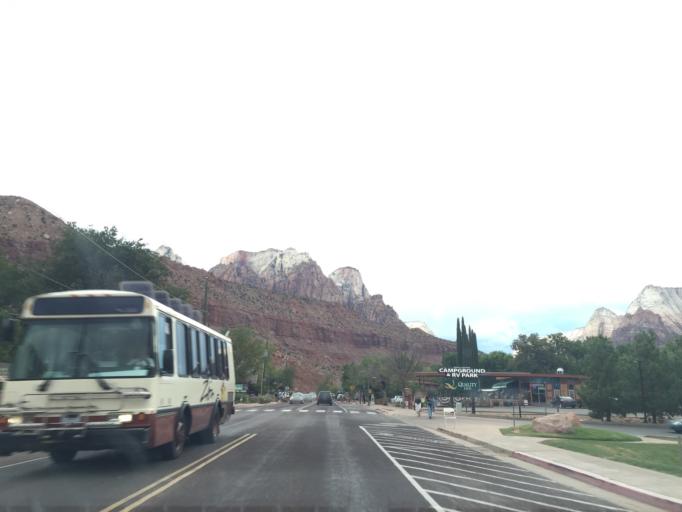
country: US
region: Utah
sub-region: Washington County
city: Hildale
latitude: 37.1935
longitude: -112.9933
